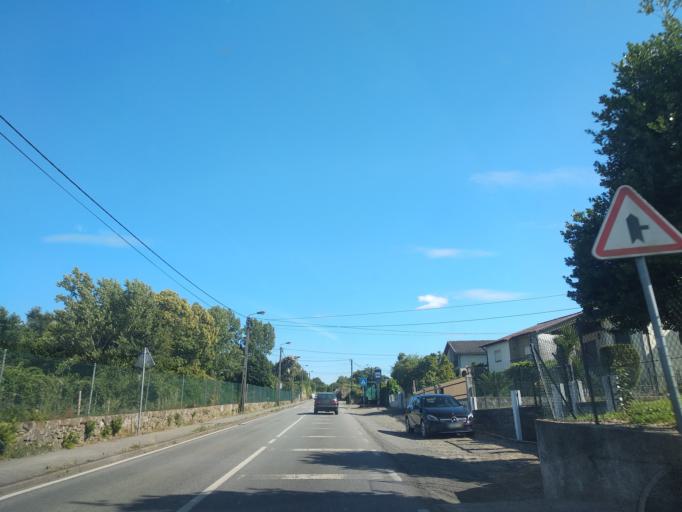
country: PT
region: Braga
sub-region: Vila Verde
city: Prado
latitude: 41.5905
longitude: -8.4588
